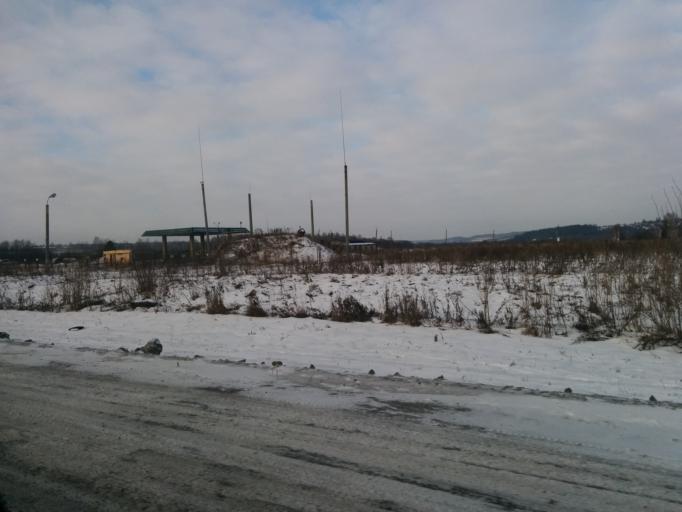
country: RU
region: Perm
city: Chaykovskaya
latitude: 58.0021
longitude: 55.4955
